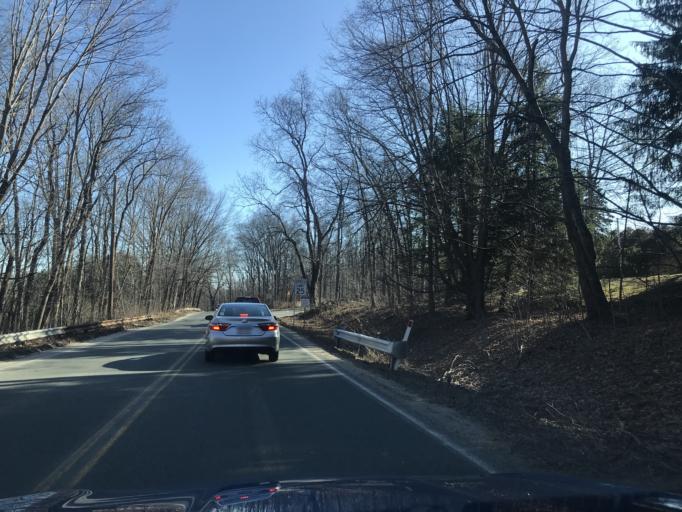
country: US
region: Massachusetts
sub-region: Essex County
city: North Andover
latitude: 42.7074
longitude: -71.0726
